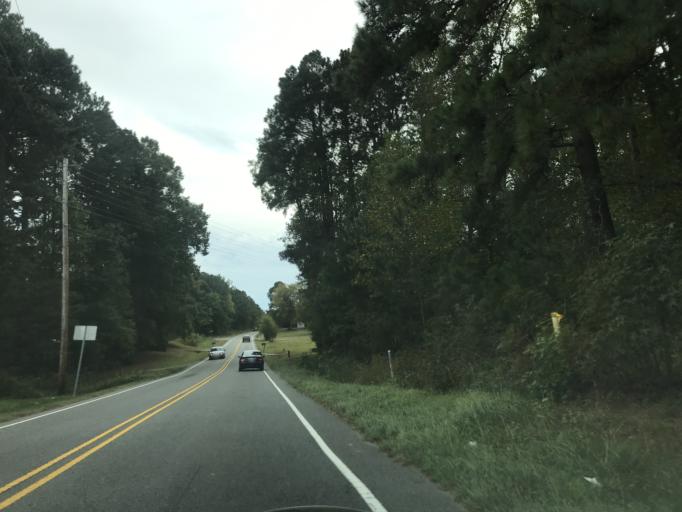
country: US
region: North Carolina
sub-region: Wake County
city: Rolesville
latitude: 35.9081
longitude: -78.5049
